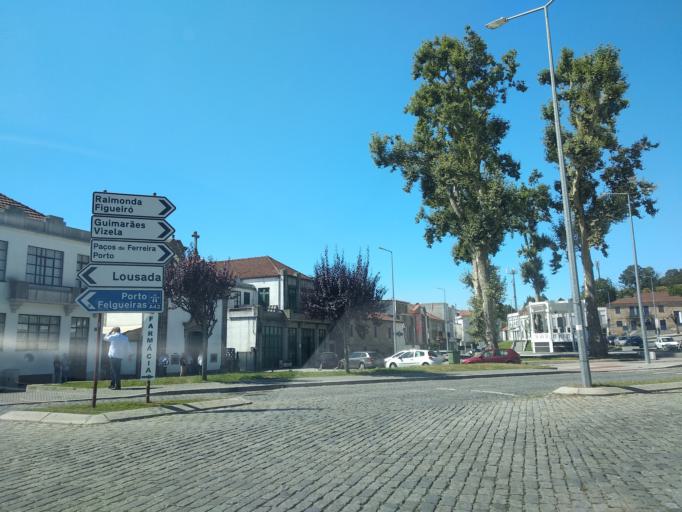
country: PT
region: Porto
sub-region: Pacos de Ferreira
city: Freamunde
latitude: 41.2889
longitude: -8.3394
